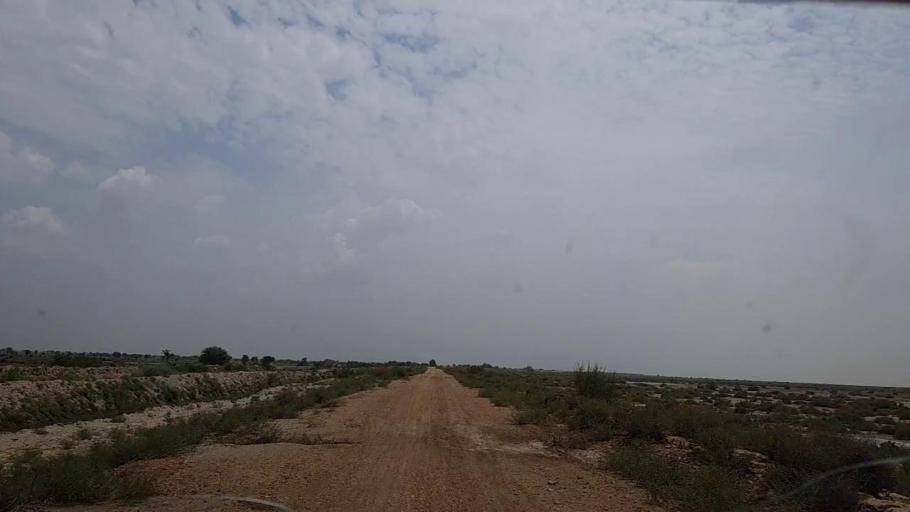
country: PK
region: Sindh
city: Phulji
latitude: 26.8379
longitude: 67.6179
